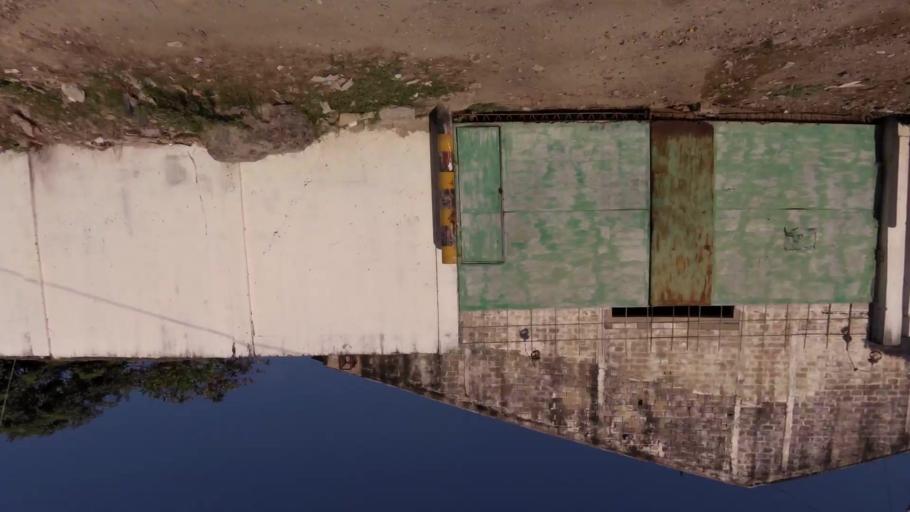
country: CO
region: Bolivar
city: Cartagena
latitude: 10.3879
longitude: -75.5238
